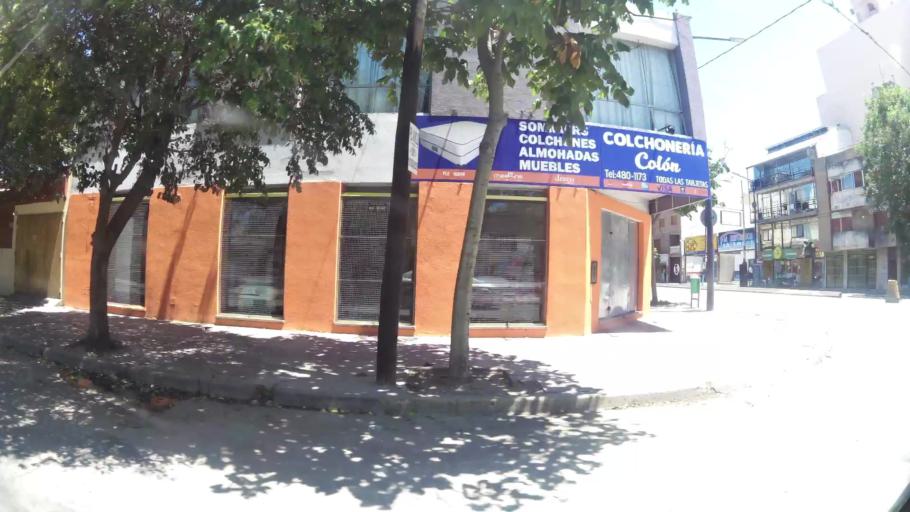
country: AR
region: Cordoba
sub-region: Departamento de Capital
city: Cordoba
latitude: -31.4039
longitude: -64.2161
